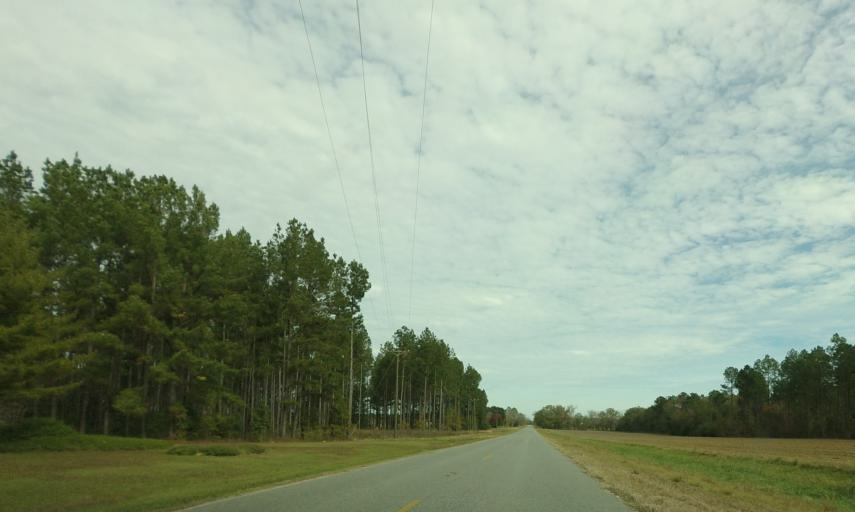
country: US
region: Georgia
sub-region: Dodge County
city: Chester
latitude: 32.4416
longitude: -83.1600
